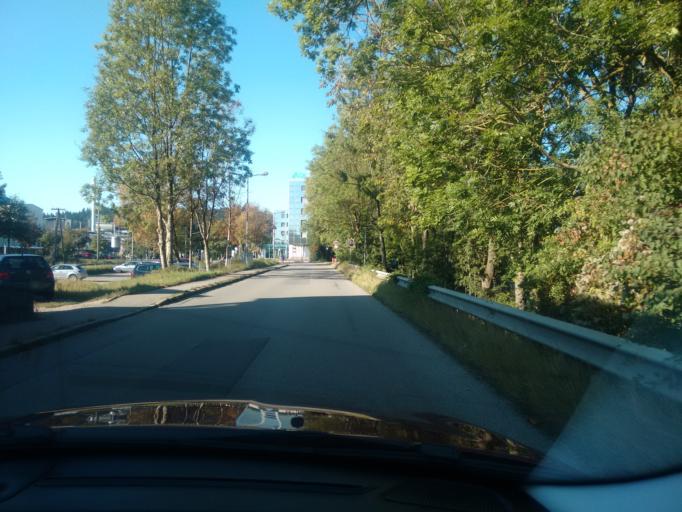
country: DE
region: Bavaria
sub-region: Upper Bavaria
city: Trostberg an der Alz
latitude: 48.0214
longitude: 12.5516
